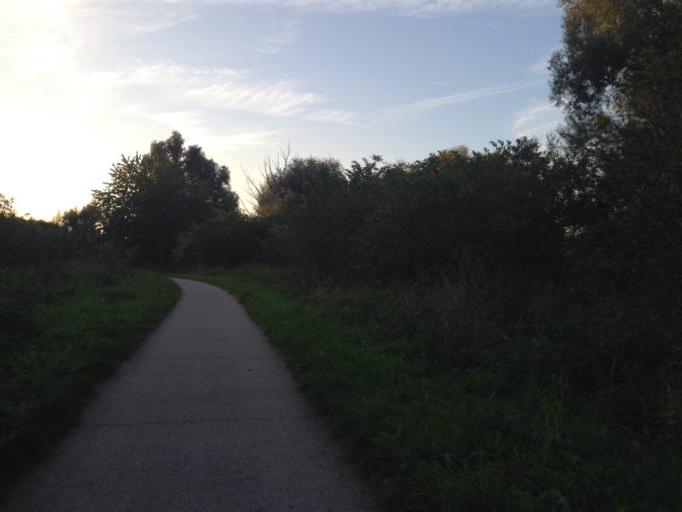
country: NL
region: Flevoland
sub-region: Gemeente Almere
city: Almere Stad
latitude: 52.4117
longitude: 5.3299
